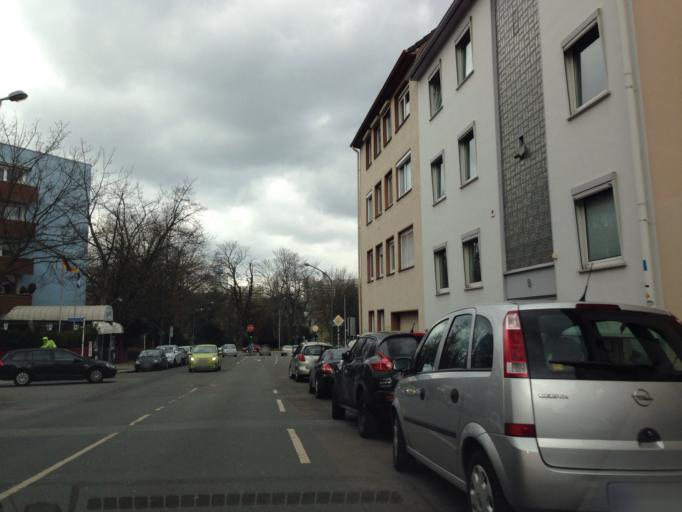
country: DE
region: North Rhine-Westphalia
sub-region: Regierungsbezirk Dusseldorf
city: Essen
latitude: 51.4418
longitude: 7.0119
